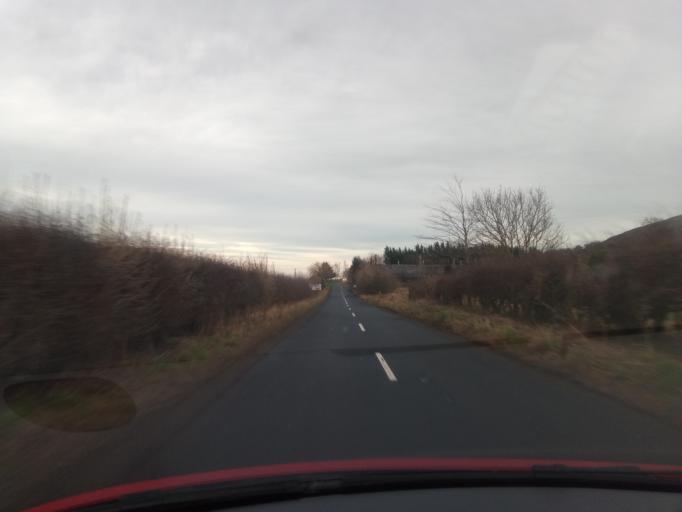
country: GB
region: England
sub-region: Northumberland
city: Kirknewton
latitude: 55.5614
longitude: -2.0730
